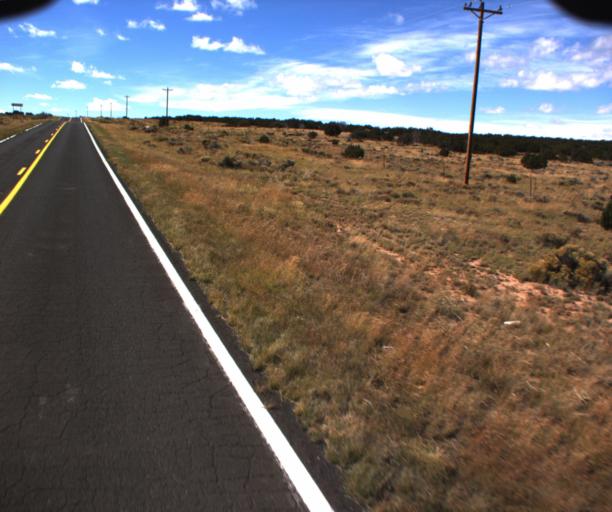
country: US
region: New Mexico
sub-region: McKinley County
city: Zuni Pueblo
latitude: 34.9724
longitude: -109.1391
